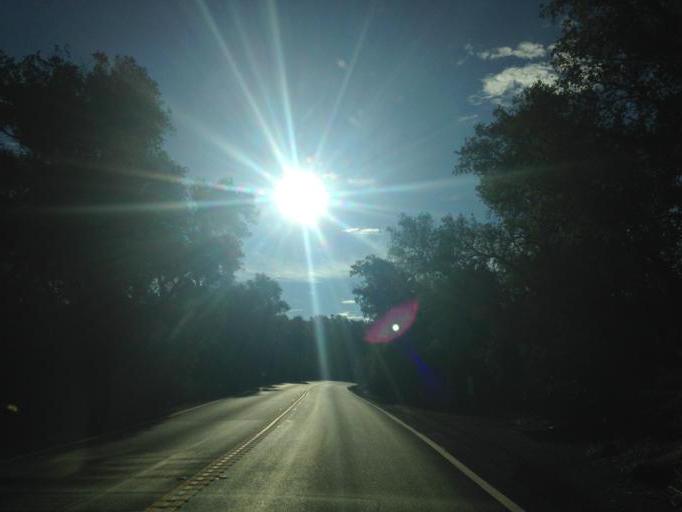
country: US
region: California
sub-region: San Diego County
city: Valley Center
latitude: 33.3018
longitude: -116.9122
